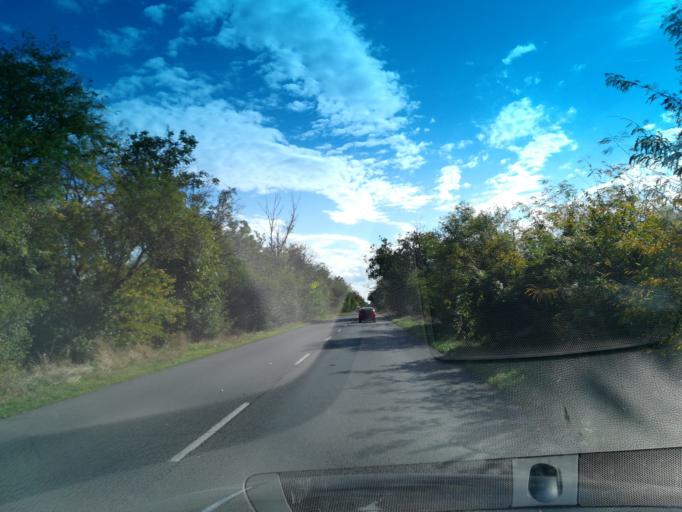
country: BG
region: Stara Zagora
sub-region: Obshtina Stara Zagora
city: Stara Zagora
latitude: 42.3714
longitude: 25.6529
